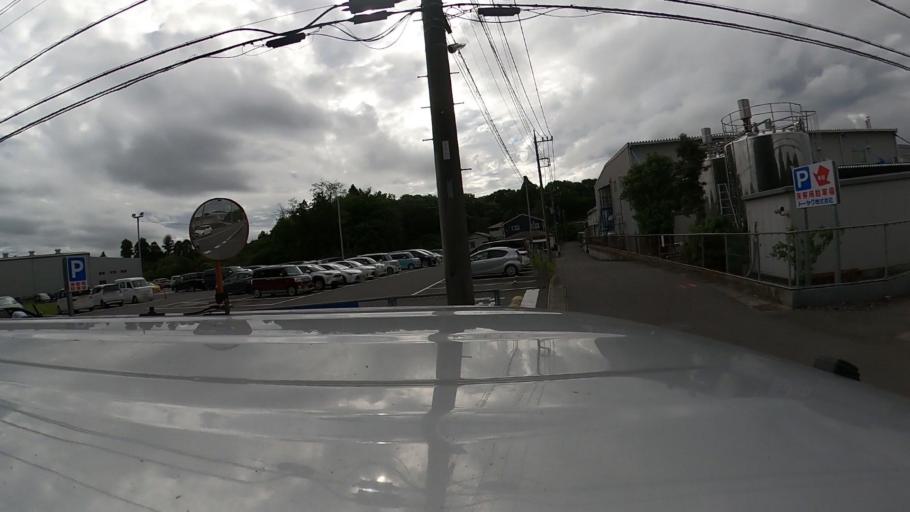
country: JP
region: Ibaraki
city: Inashiki
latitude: 36.0041
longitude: 140.2843
